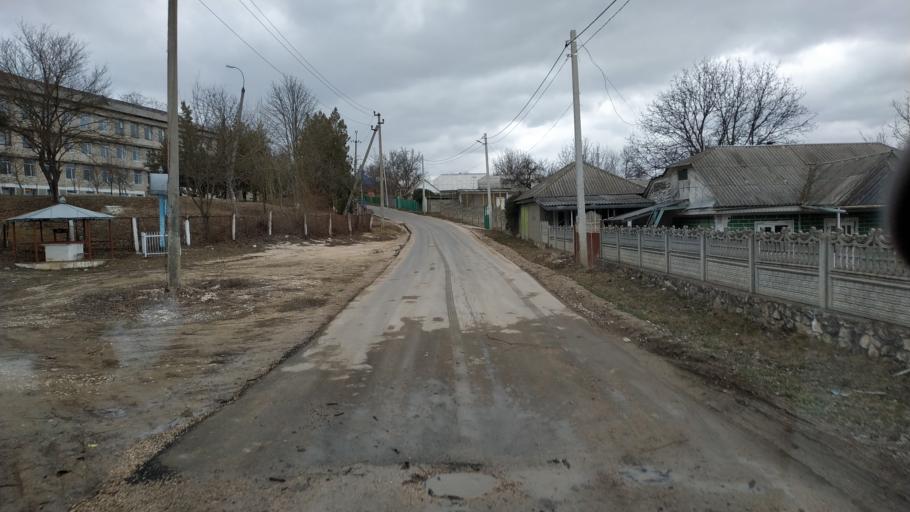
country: MD
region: Calarasi
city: Calarasi
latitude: 47.2383
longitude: 28.3104
